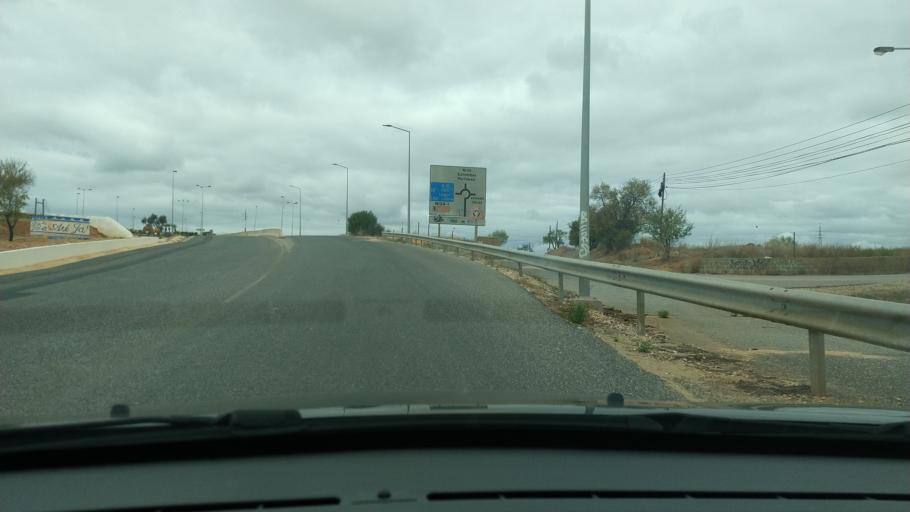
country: PT
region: Faro
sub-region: Lagoa
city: Lagoa
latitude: 37.1424
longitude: -8.4525
